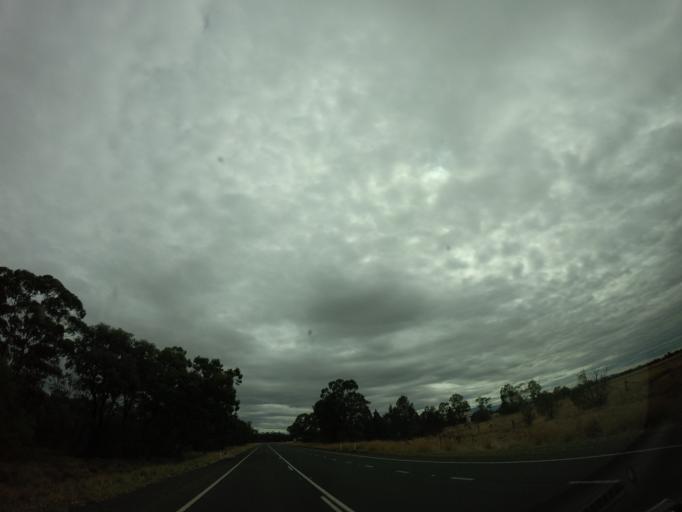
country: AU
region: New South Wales
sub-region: Narrabri
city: Narrabri
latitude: -30.3573
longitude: 149.7437
